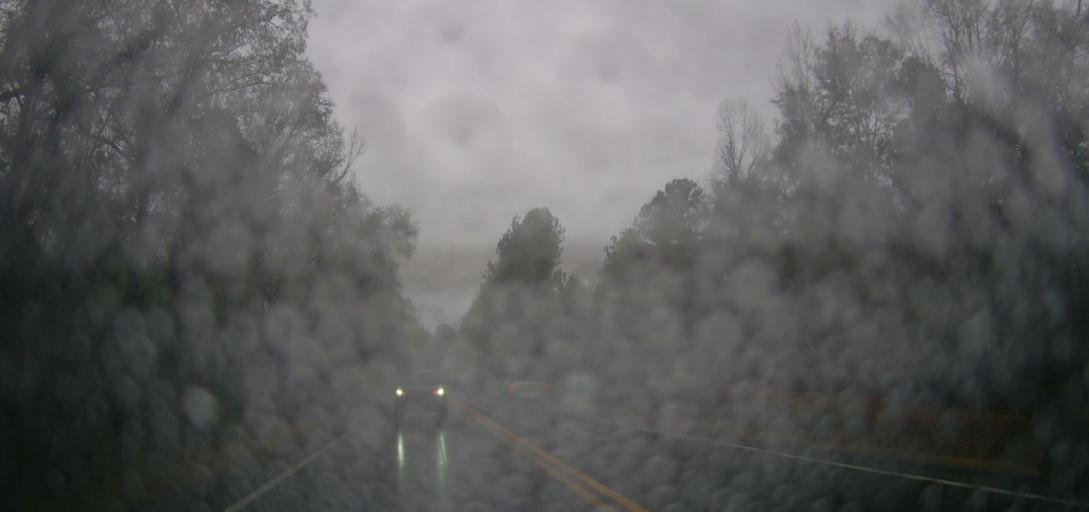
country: US
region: Georgia
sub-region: Putnam County
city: Eatonton
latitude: 33.2234
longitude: -83.4304
